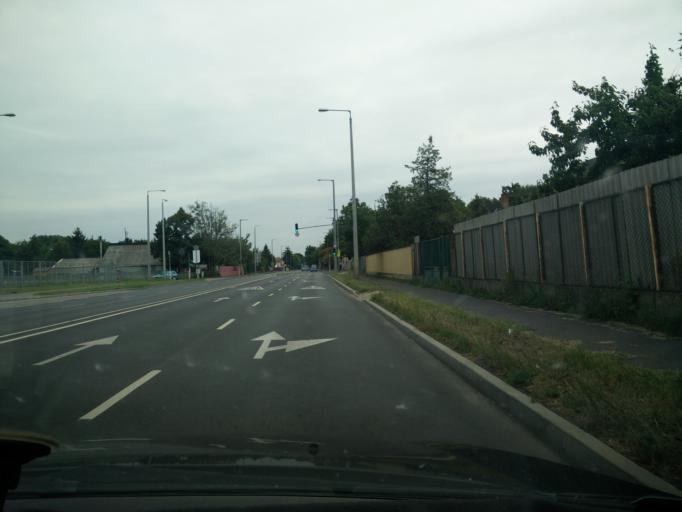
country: HU
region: Hajdu-Bihar
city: Debrecen
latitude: 47.5289
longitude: 21.6532
